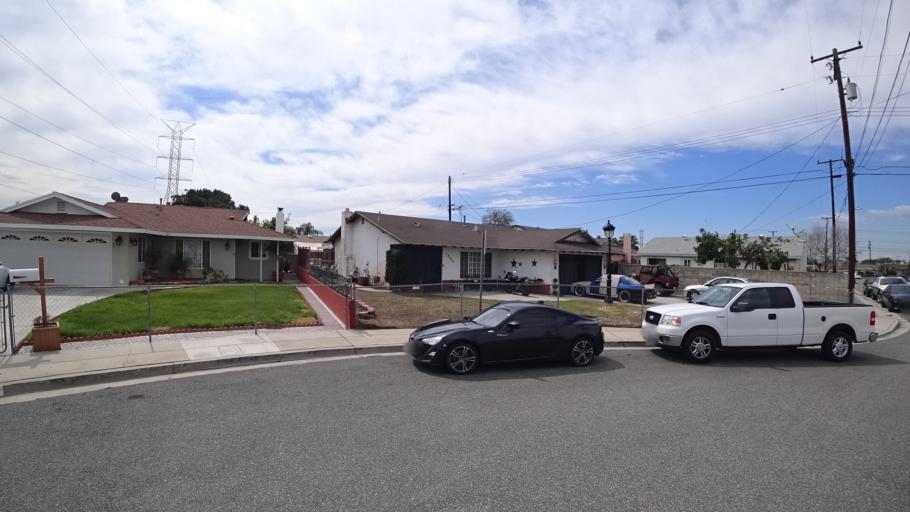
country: US
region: California
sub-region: Los Angeles County
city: West Puente Valley
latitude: 34.0738
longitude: -117.9927
